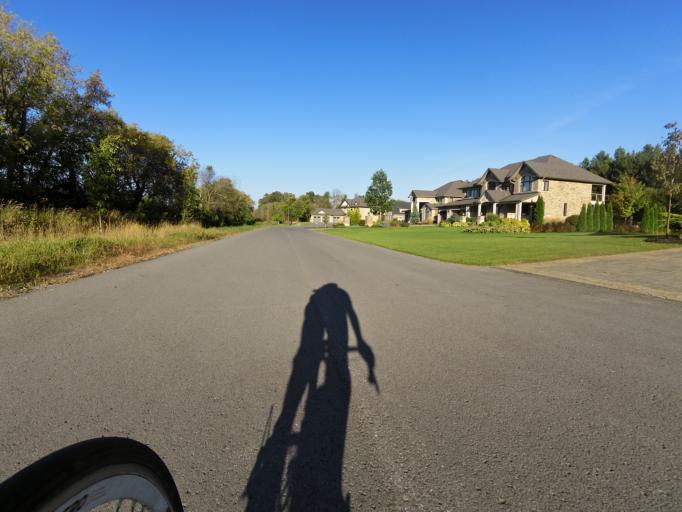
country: CA
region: Ontario
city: Bells Corners
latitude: 45.2103
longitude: -75.7039
